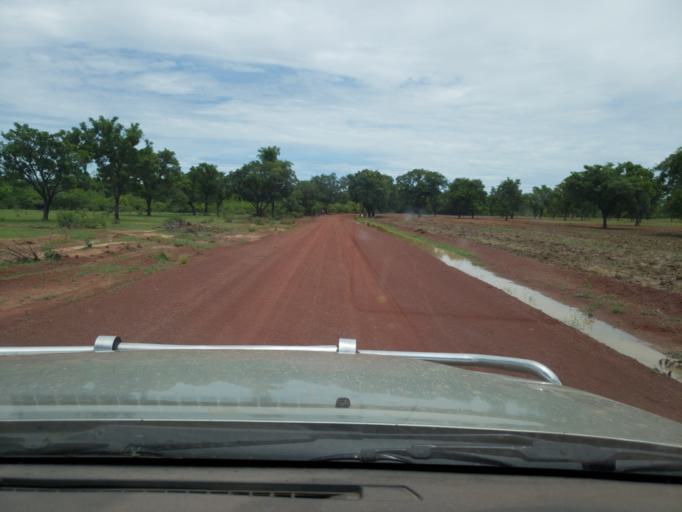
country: ML
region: Sikasso
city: Sikasso
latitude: 11.6817
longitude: -6.3276
